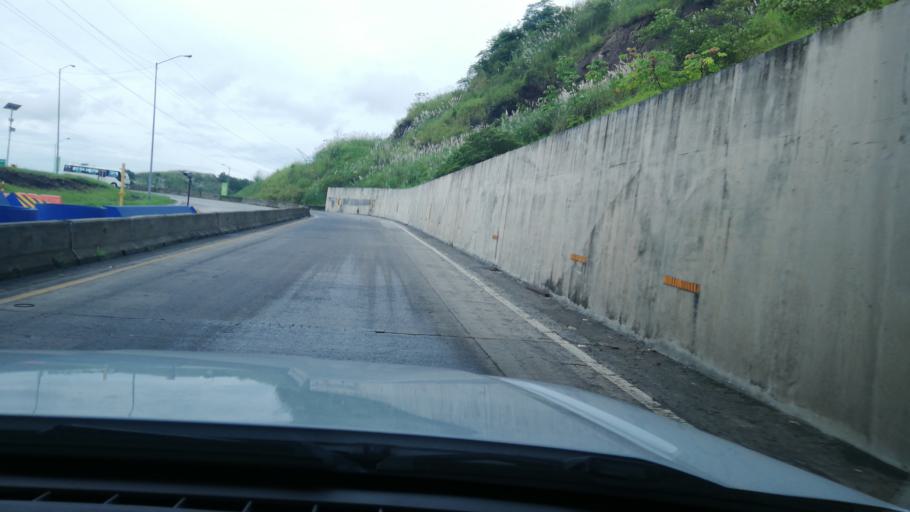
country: PA
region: Panama
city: Las Cumbres
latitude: 9.0598
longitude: -79.5106
